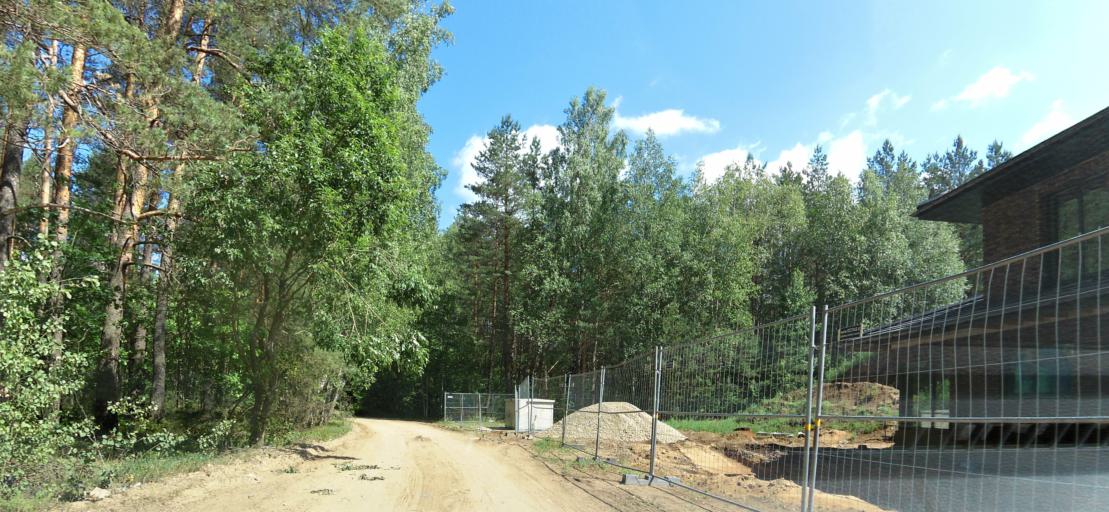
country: LT
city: Nemencine
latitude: 54.8154
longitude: 25.3884
